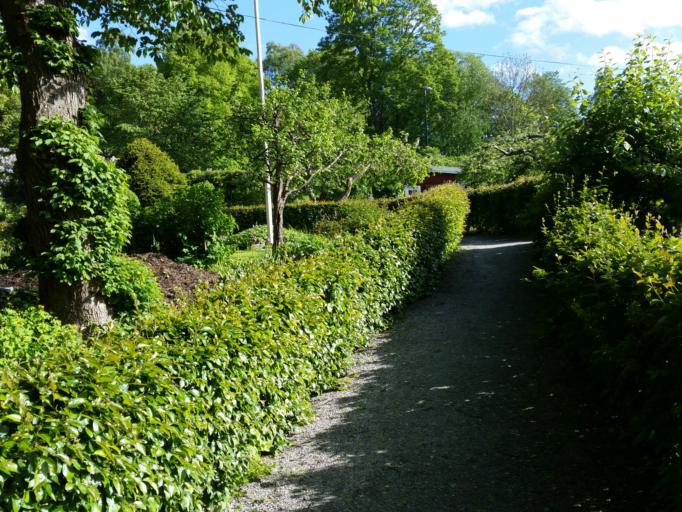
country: SE
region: Stockholm
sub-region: Stockholms Kommun
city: Arsta
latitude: 59.3150
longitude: 18.0467
